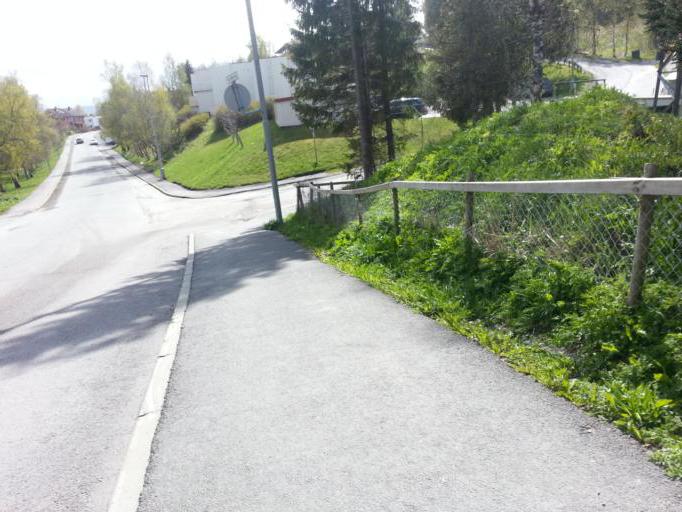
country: NO
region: Sor-Trondelag
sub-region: Trondheim
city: Trondheim
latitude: 63.3946
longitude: 10.3541
